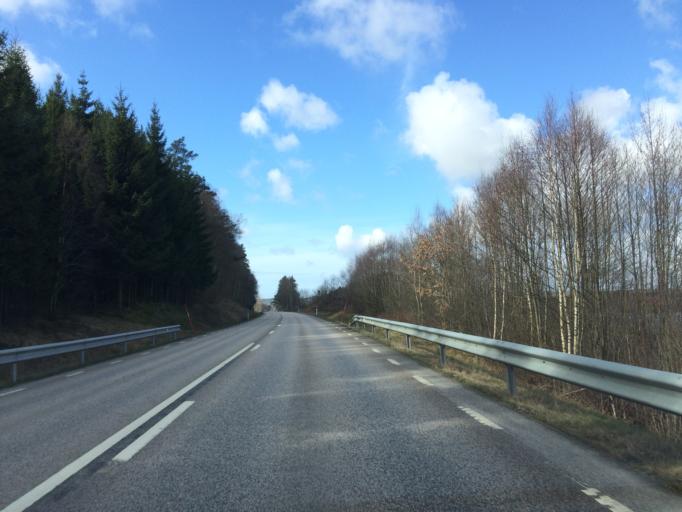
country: SE
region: Halland
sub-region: Laholms Kommun
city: Knared
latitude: 56.5033
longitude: 13.3560
